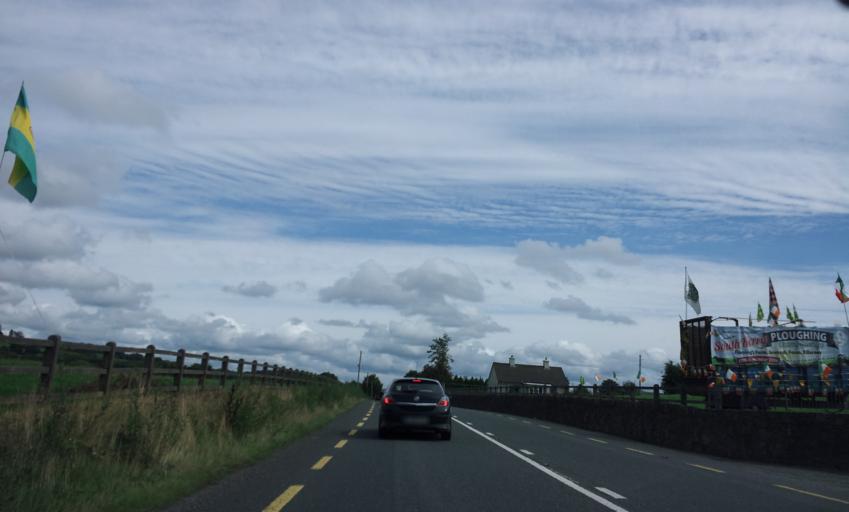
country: IE
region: Munster
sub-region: Ciarrai
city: Cill Airne
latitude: 52.0720
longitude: -9.6092
